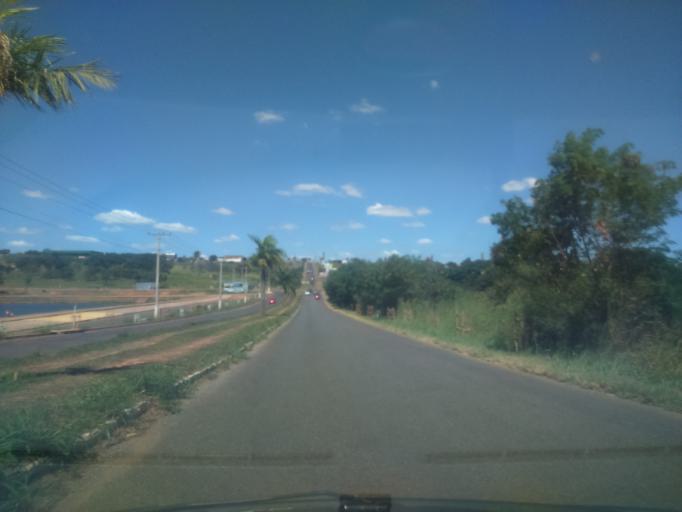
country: BR
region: Goias
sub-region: Luziania
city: Luziania
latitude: -16.1107
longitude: -47.9414
